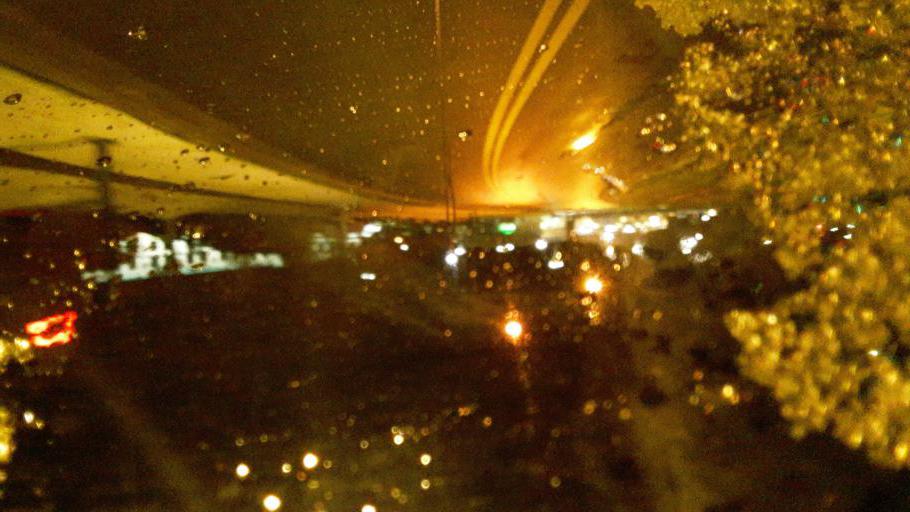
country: US
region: Ohio
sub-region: Portage County
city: Streetsboro
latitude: 41.2495
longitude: -81.3658
